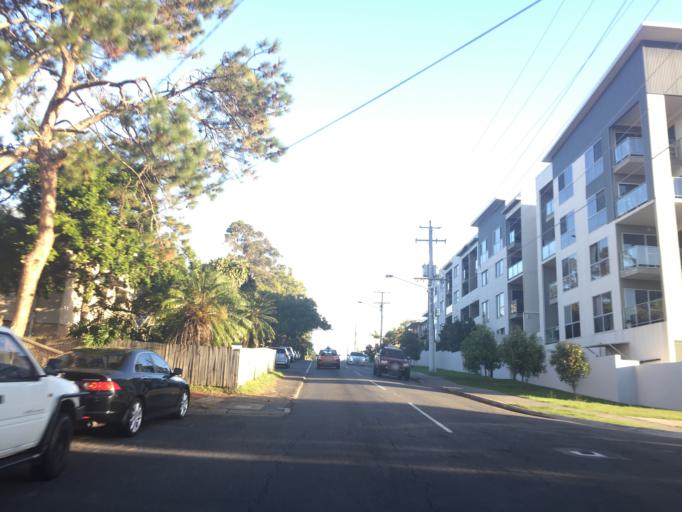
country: AU
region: Queensland
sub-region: Brisbane
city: Wavell Heights
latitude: -27.4048
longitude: 153.0645
